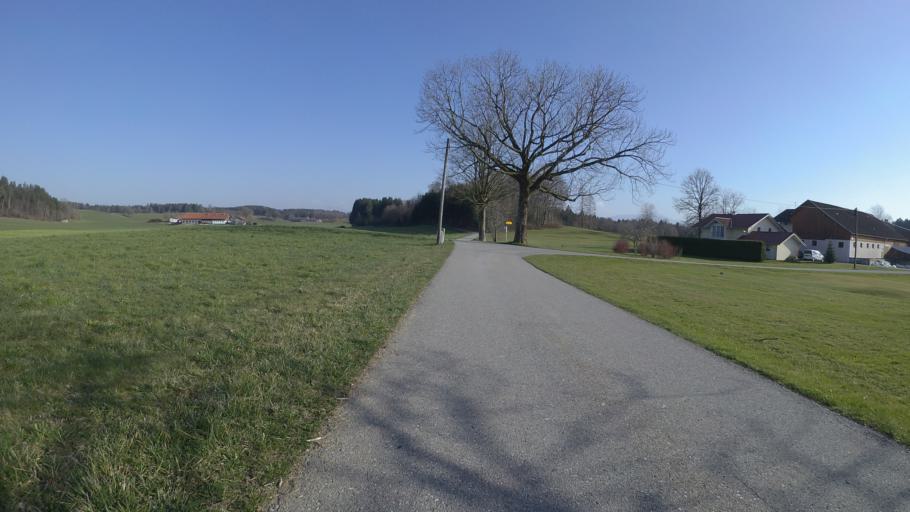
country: DE
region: Bavaria
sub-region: Upper Bavaria
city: Traunreut
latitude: 47.9340
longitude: 12.5618
